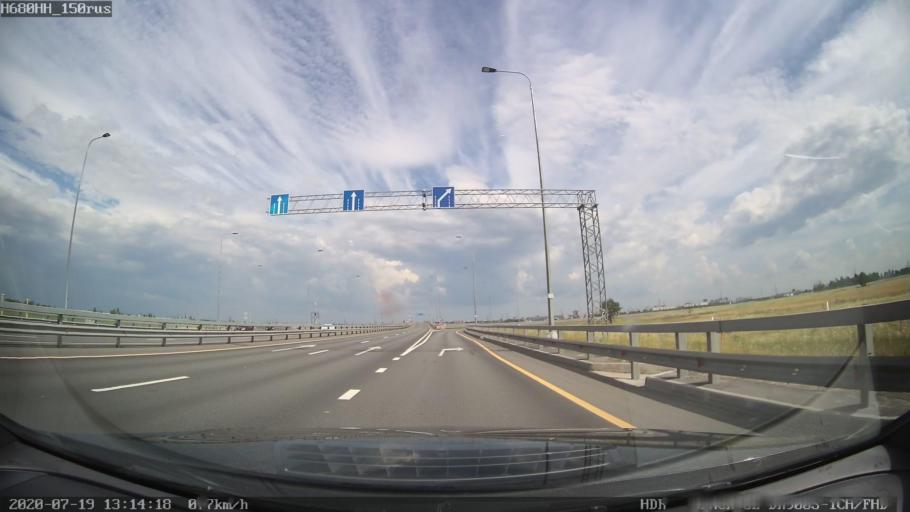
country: RU
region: Leningrad
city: Fedorovskoye
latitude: 59.7304
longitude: 30.5212
